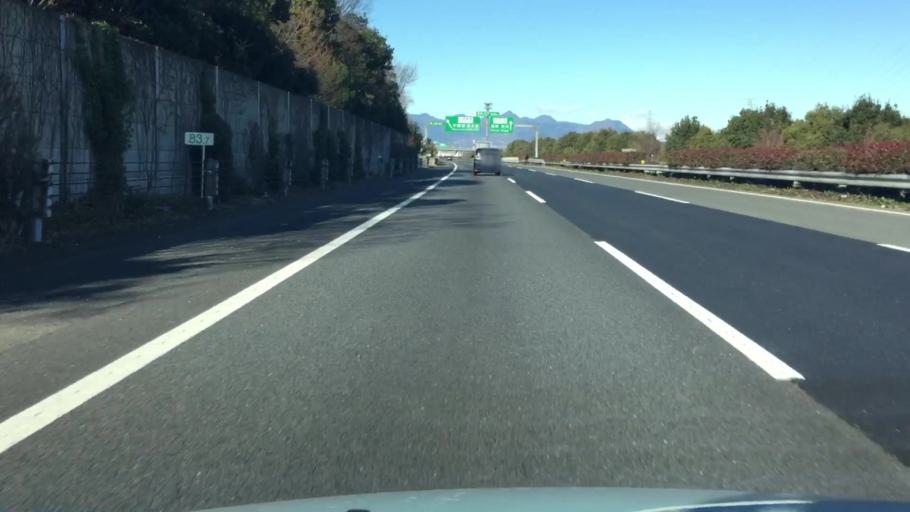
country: JP
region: Gunma
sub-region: Sawa-gun
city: Tamamura
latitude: 36.3150
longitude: 139.0841
